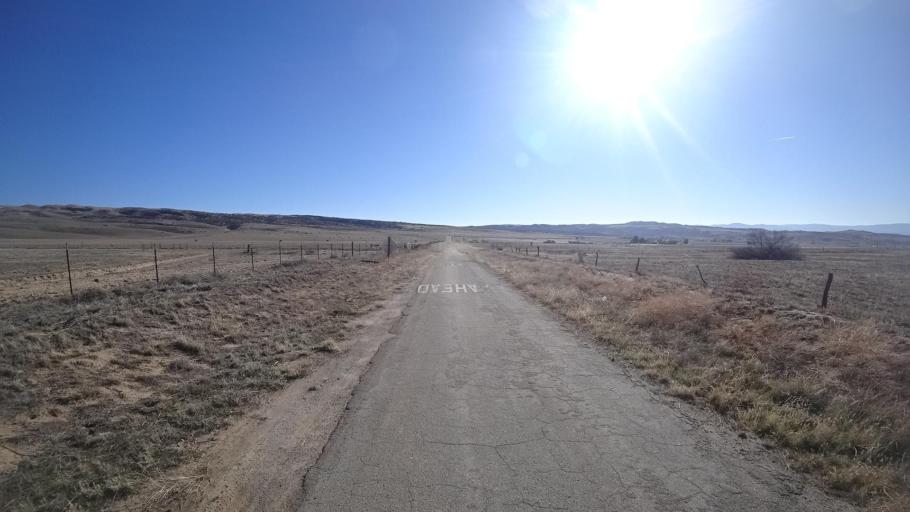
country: US
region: California
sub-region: Kern County
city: Maricopa
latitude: 34.9461
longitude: -119.4553
